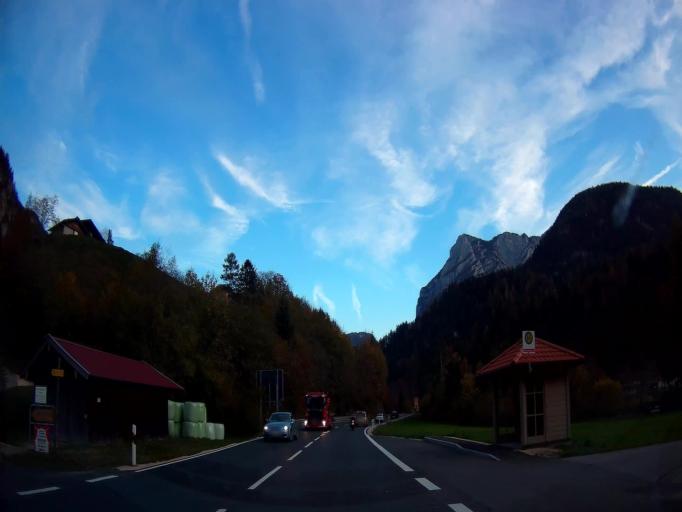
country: DE
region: Bavaria
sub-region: Upper Bavaria
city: Schneizlreuth
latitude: 47.6892
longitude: 12.8038
